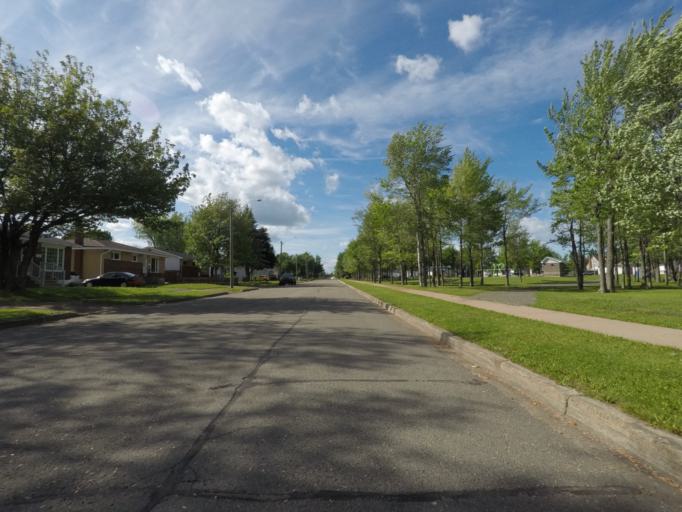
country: CA
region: New Brunswick
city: Moncton
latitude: 46.0993
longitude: -64.8249
